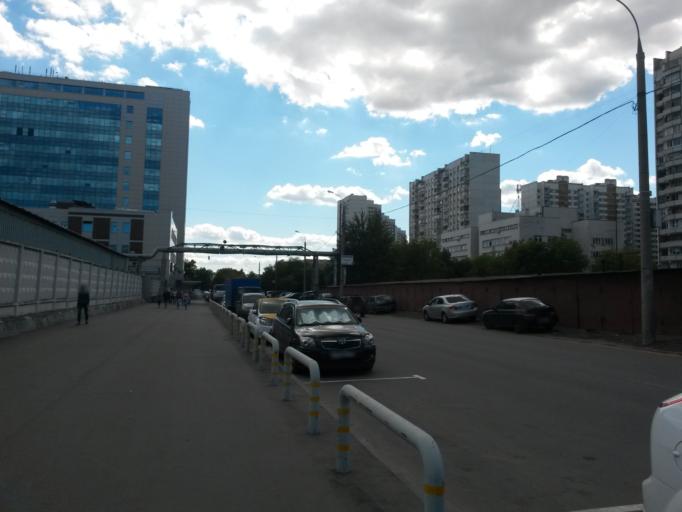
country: RU
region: Moskovskaya
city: Kozhukhovo
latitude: 55.7036
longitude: 37.6897
